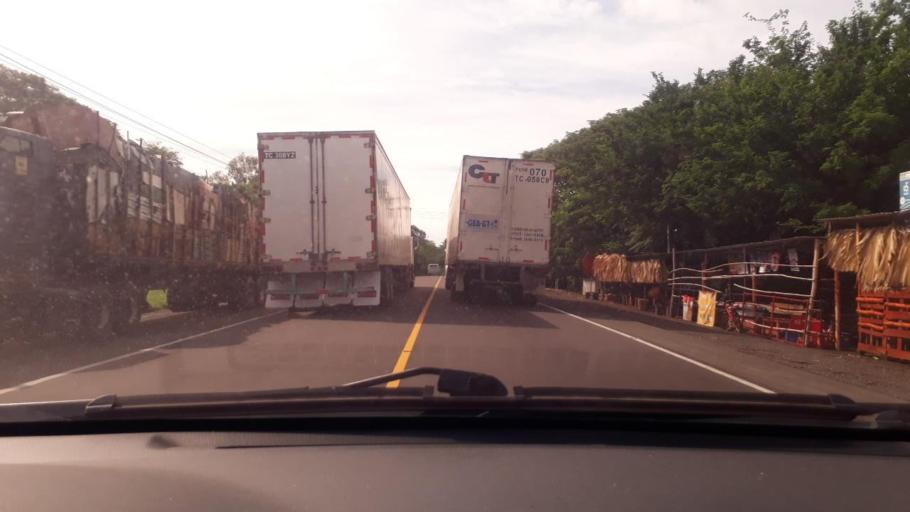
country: GT
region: Jutiapa
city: Pasaco
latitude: 13.8886
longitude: -90.1439
